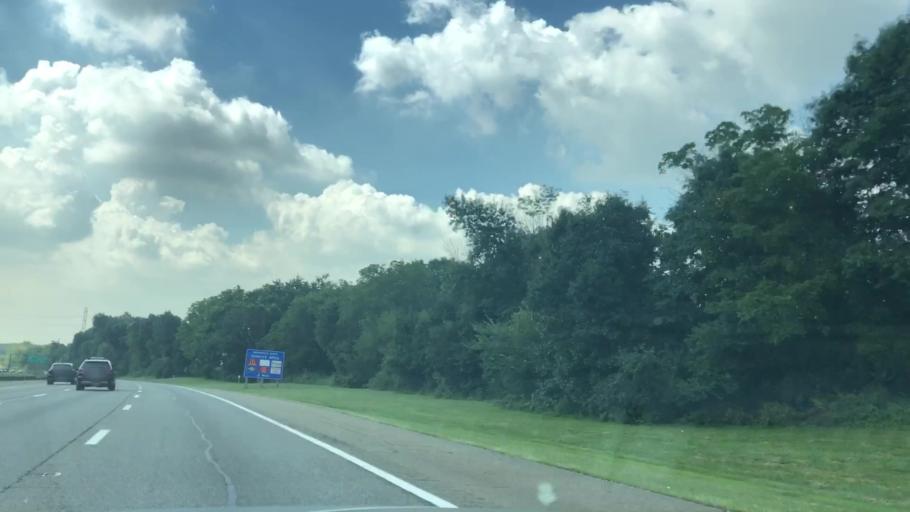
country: US
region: New Jersey
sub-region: Passaic County
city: Clifton
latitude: 40.8644
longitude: -74.1723
